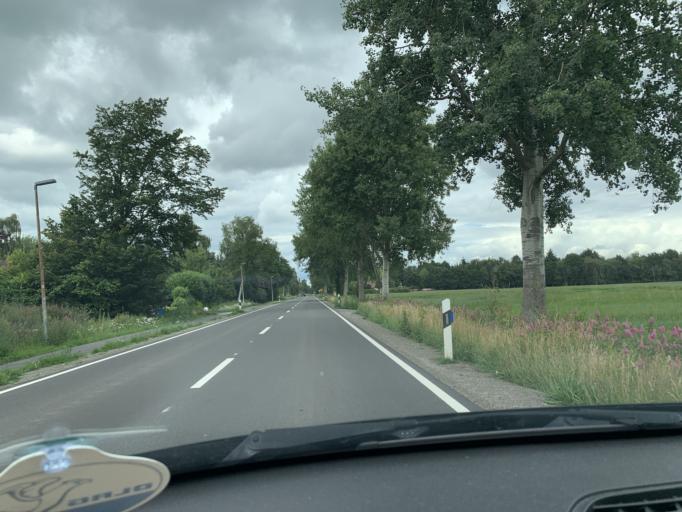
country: DE
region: Lower Saxony
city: Edewecht
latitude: 53.0888
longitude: 7.9910
